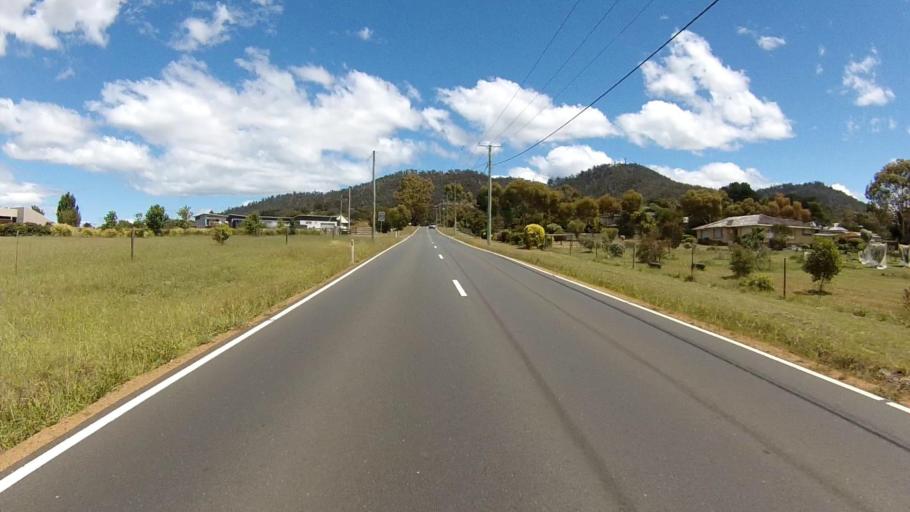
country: AU
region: Tasmania
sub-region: Clarence
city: Seven Mile Beach
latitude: -42.8508
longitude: 147.4753
